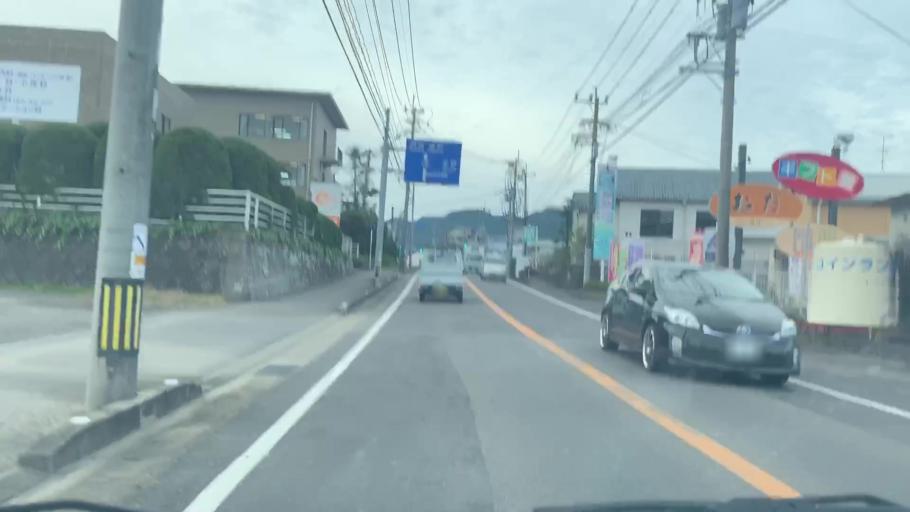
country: JP
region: Saga Prefecture
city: Kashima
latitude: 33.1337
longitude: 130.0620
